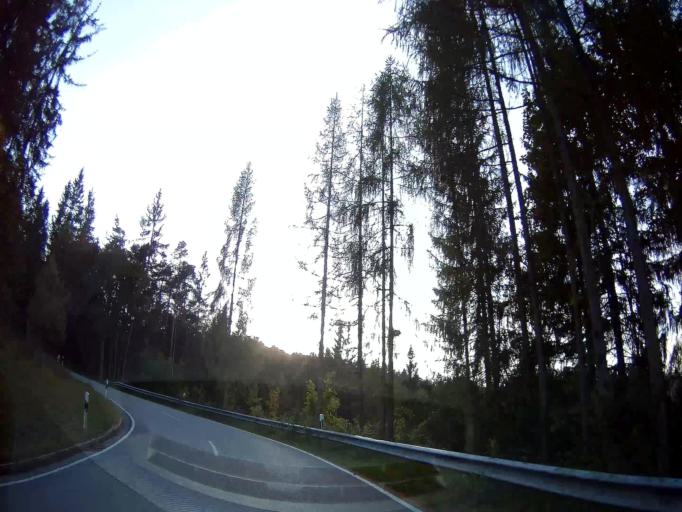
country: DE
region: Bavaria
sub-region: Upper Bavaria
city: Bischofswiesen
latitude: 47.6537
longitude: 12.9467
